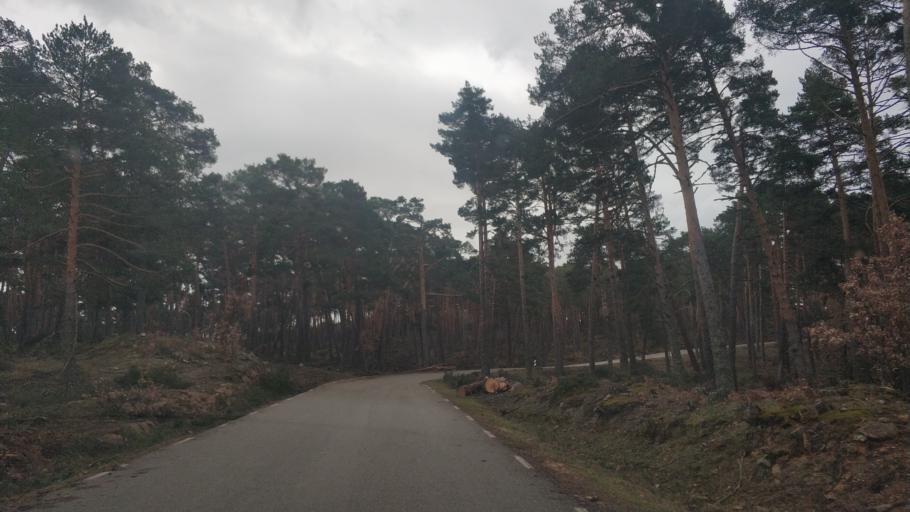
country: ES
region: Castille and Leon
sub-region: Provincia de Burgos
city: Canicosa de la Sierra
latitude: 41.9166
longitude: -3.0372
